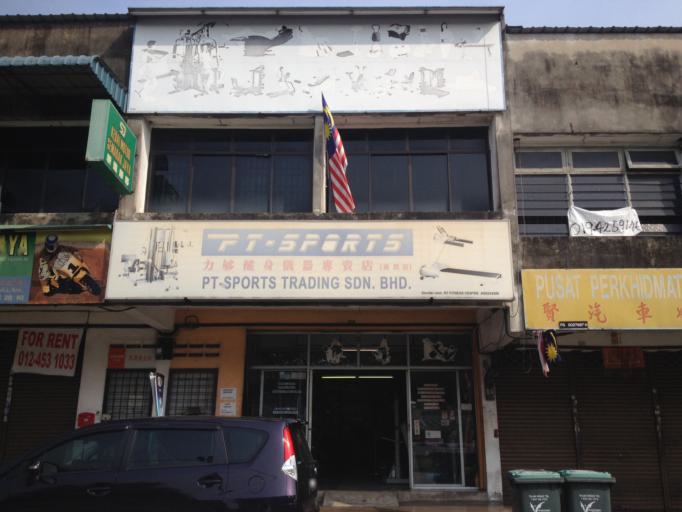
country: MY
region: Kedah
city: Kulim
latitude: 5.3790
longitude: 100.5427
